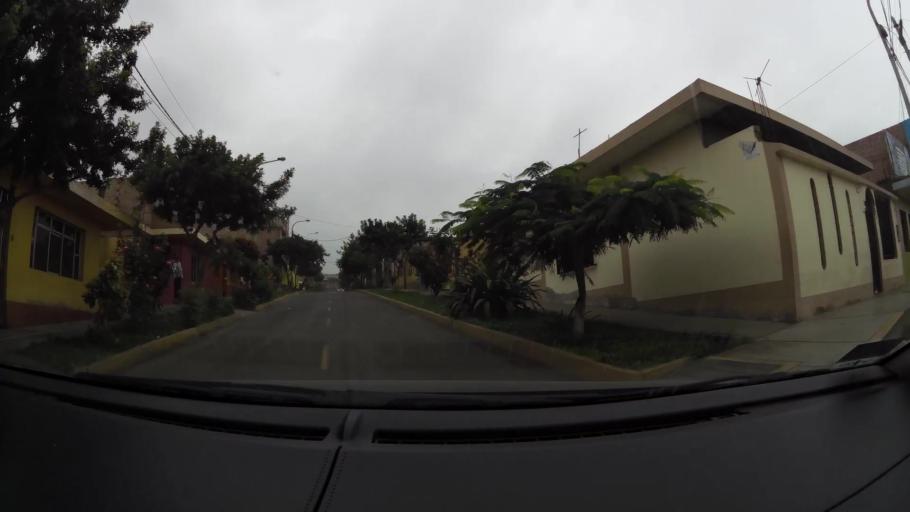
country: PE
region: Lima
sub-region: Provincia de Huaral
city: Chancay
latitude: -11.5924
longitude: -77.2586
